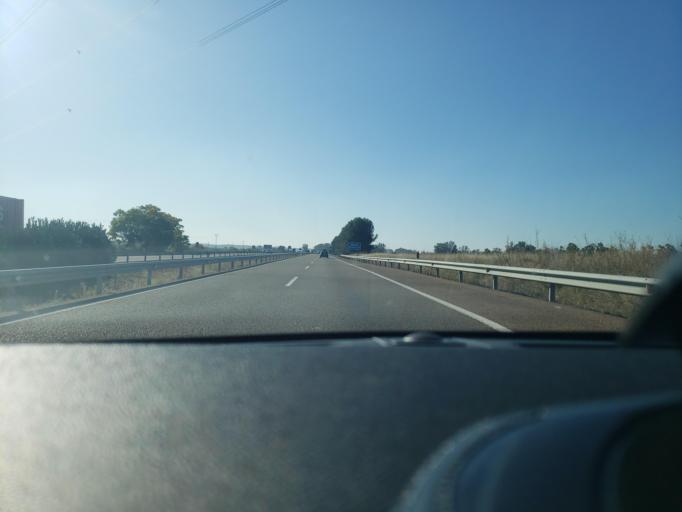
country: ES
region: Extremadura
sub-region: Provincia de Badajoz
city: Arroyo de San Servan
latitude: 38.8730
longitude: -6.4851
